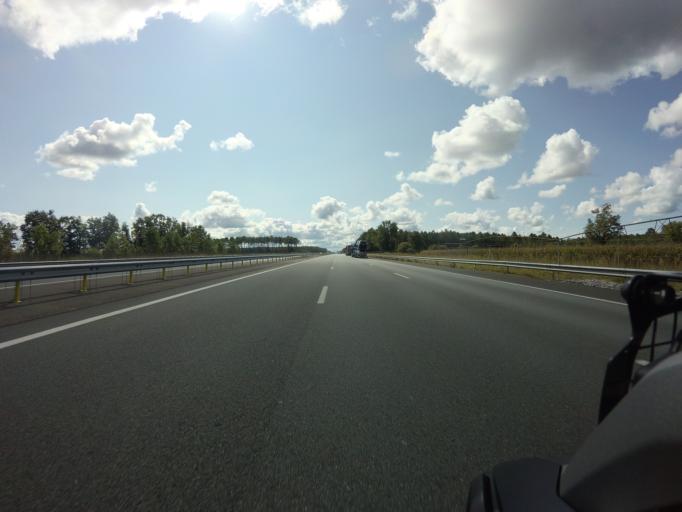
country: FR
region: Aquitaine
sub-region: Departement des Landes
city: Saint-Geours-de-Maremne
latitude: 43.7351
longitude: -1.2268
